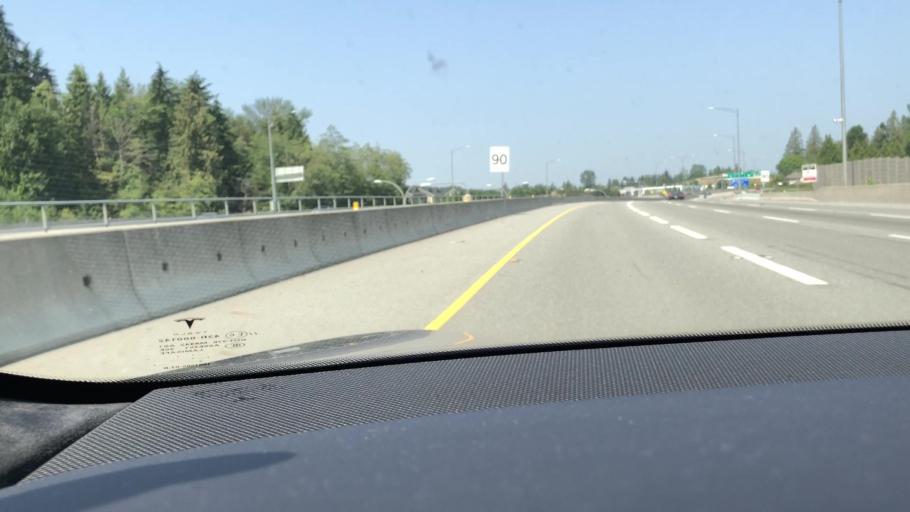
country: CA
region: British Columbia
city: Coquitlam
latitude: 49.1951
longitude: -122.7884
